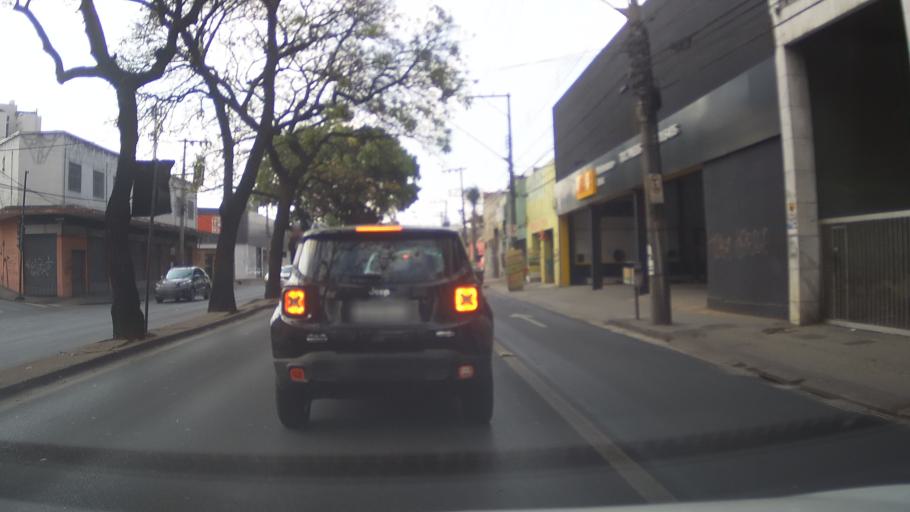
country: BR
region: Minas Gerais
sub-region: Belo Horizonte
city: Belo Horizonte
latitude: -19.9127
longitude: -43.9547
